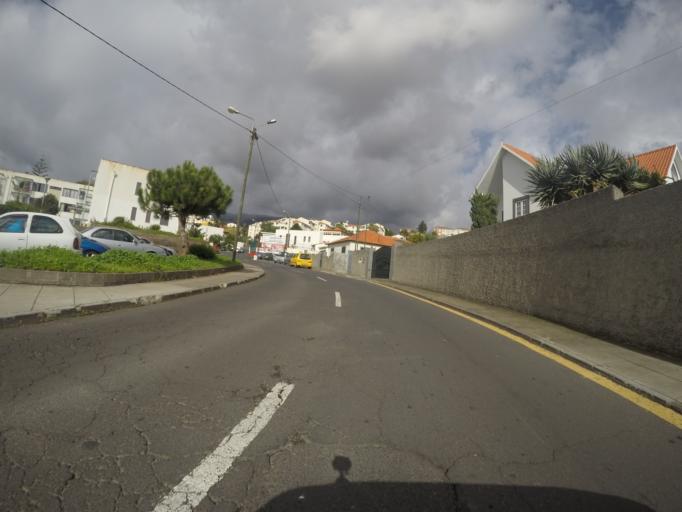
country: PT
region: Madeira
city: Camara de Lobos
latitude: 32.6577
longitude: -16.9443
